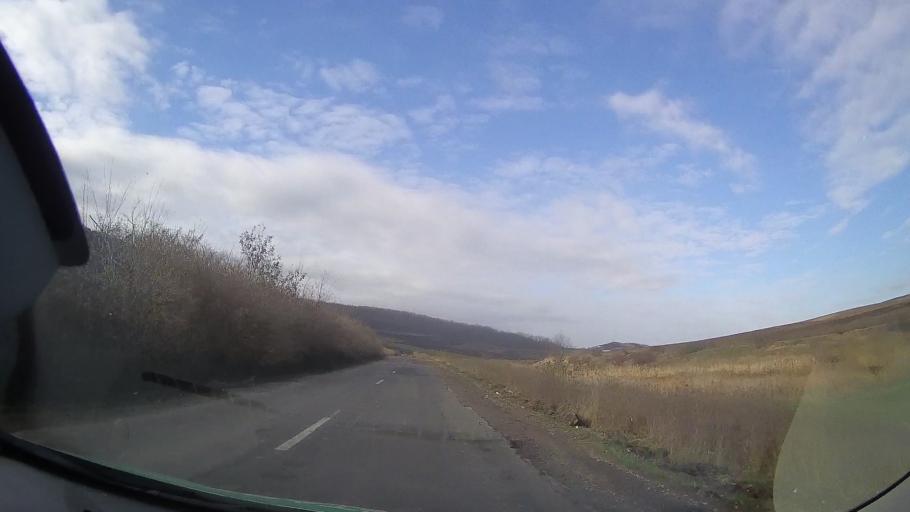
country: RO
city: Barza
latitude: 46.5541
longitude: 24.1044
